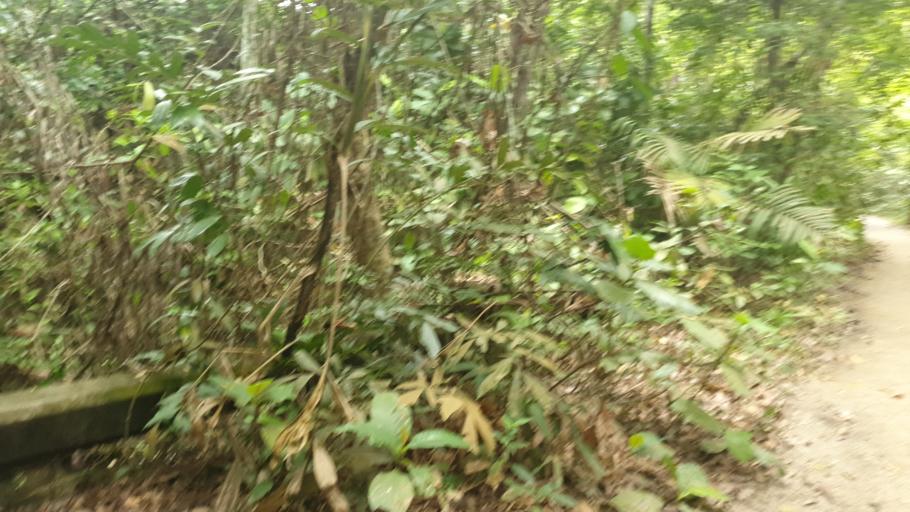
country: SG
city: Singapore
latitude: 1.3529
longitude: 103.8064
